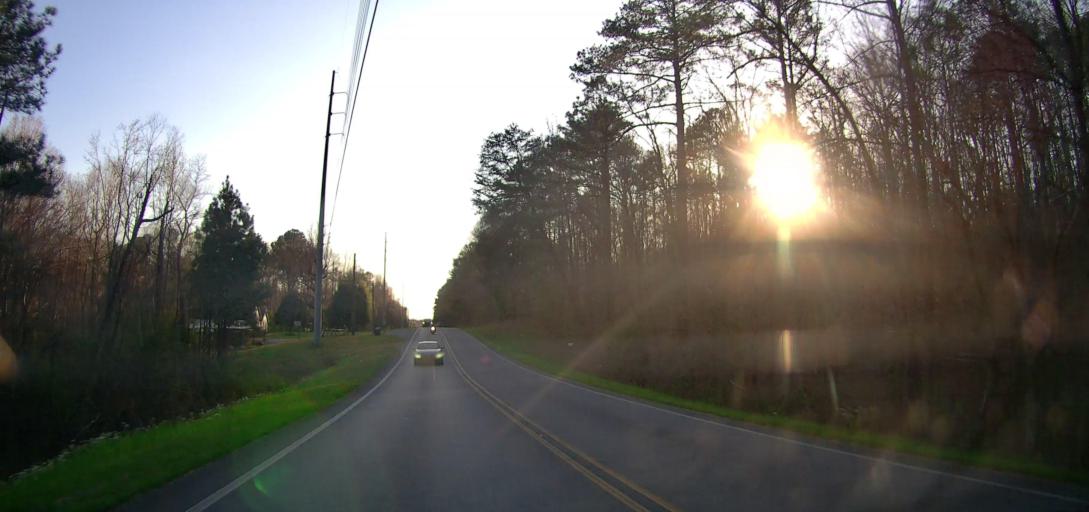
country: US
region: Alabama
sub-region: Shelby County
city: Indian Springs Village
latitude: 33.3124
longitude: -86.7321
